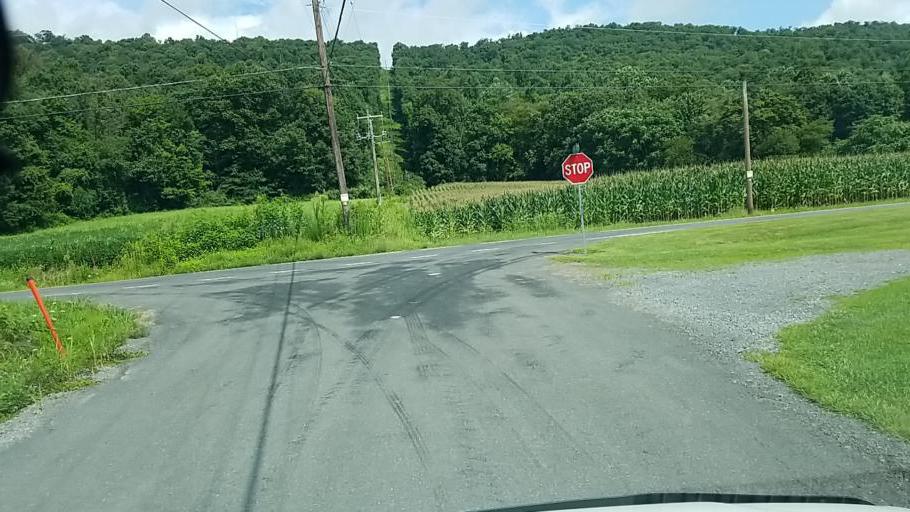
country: US
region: Pennsylvania
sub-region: Dauphin County
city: Millersburg
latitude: 40.5800
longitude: -76.9330
